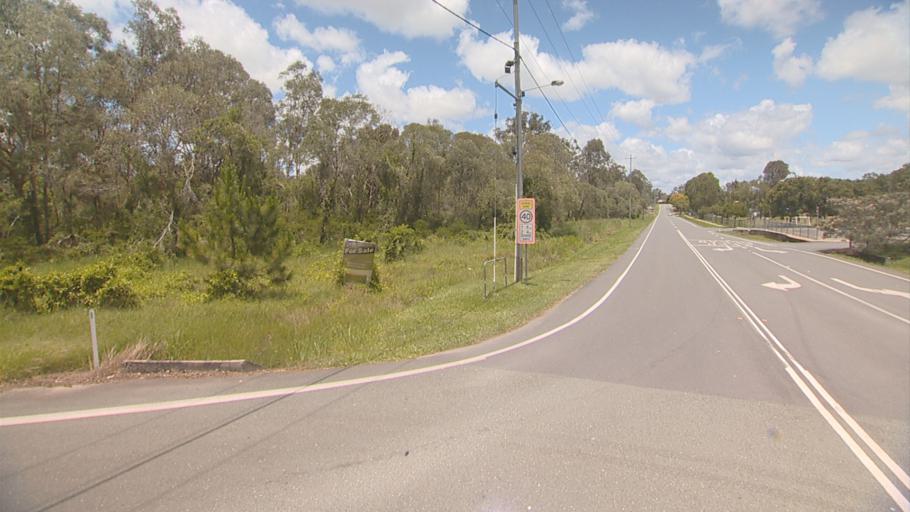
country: AU
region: Queensland
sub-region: Gold Coast
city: Yatala
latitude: -27.6776
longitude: 153.2365
